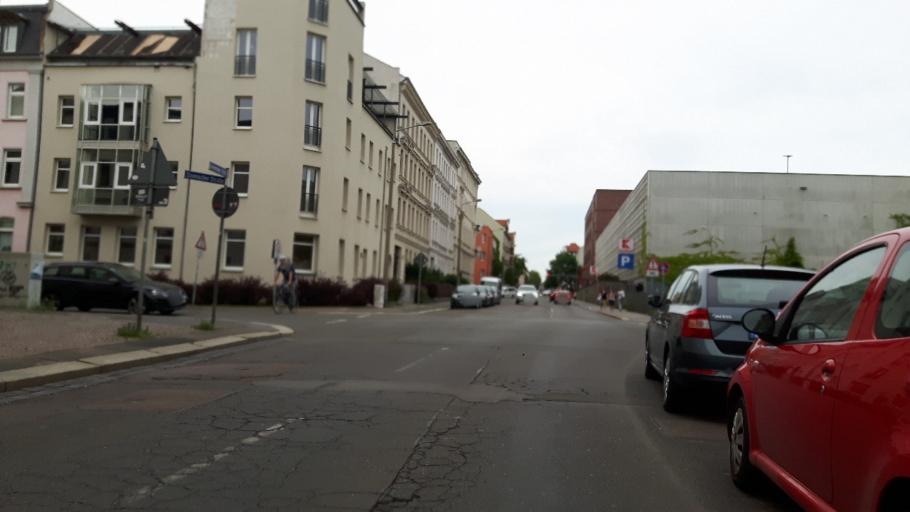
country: DE
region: Saxony
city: Leipzig
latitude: 51.3614
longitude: 12.3611
